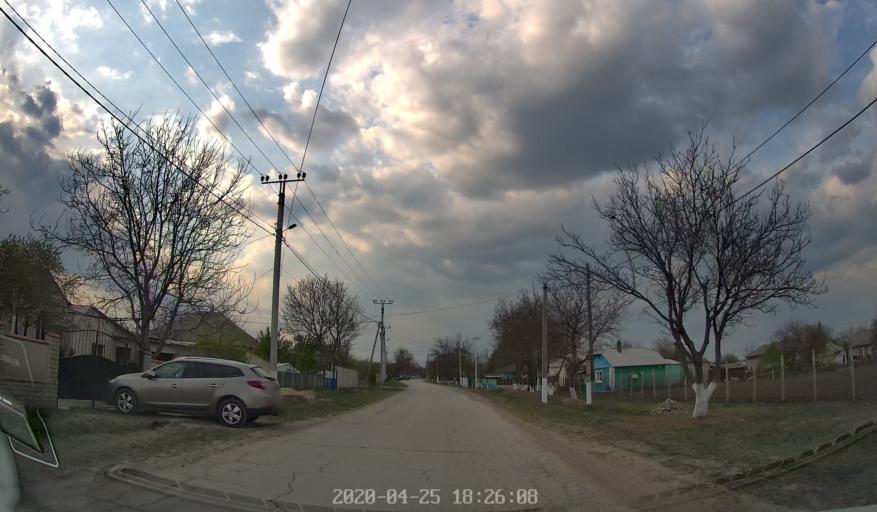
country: MD
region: Criuleni
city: Criuleni
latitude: 47.1652
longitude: 29.1273
